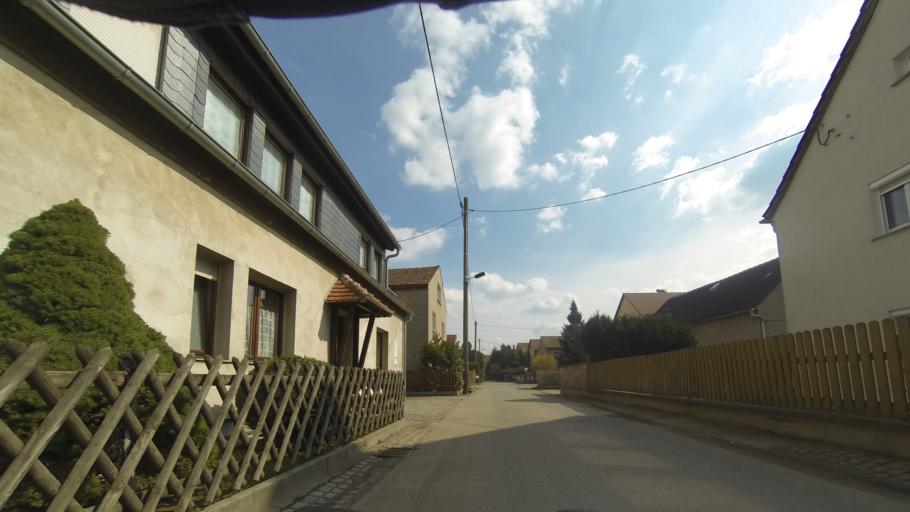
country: DE
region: Saxony
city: Moritzburg
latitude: 51.1490
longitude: 13.7366
